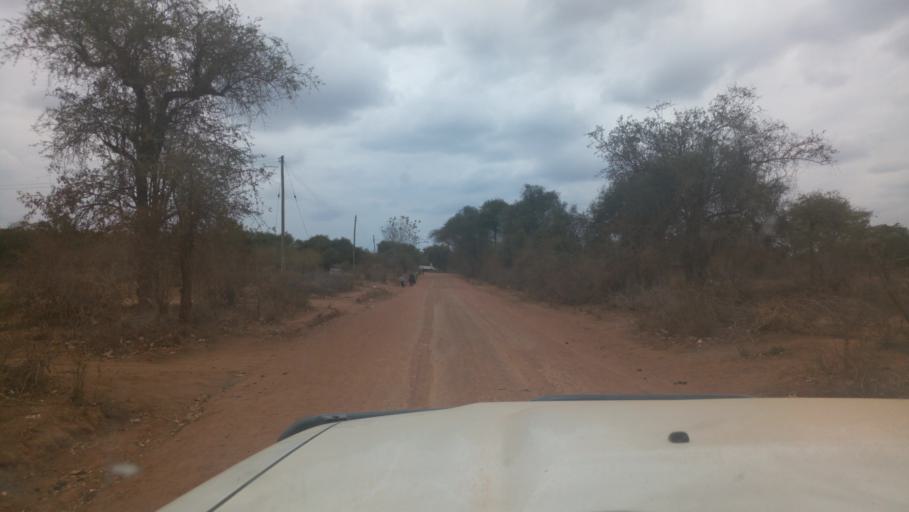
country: KE
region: Makueni
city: Wote
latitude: -1.6685
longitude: 37.8979
